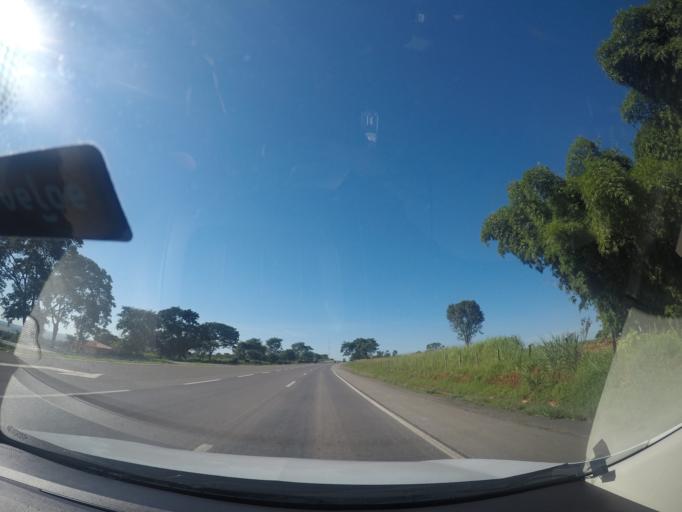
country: BR
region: Goias
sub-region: Piracanjuba
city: Piracanjuba
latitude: -17.2863
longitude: -49.2359
